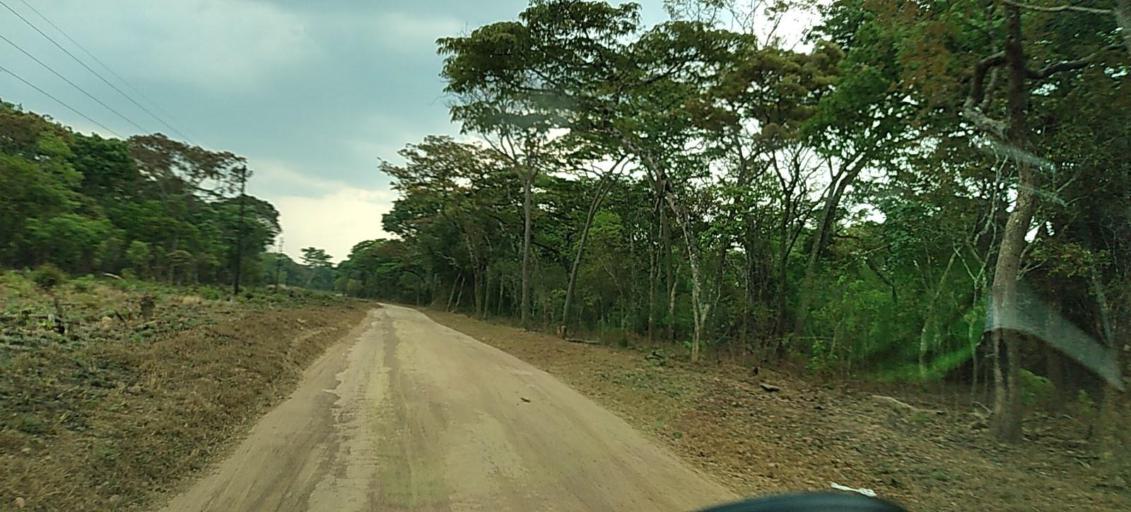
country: ZM
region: North-Western
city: Solwezi
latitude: -12.7754
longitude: 26.4724
